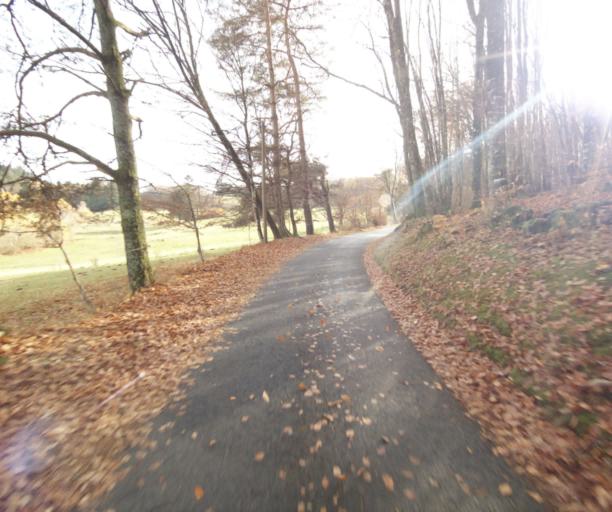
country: FR
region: Limousin
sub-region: Departement de la Correze
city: Cornil
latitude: 45.1926
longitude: 1.7257
